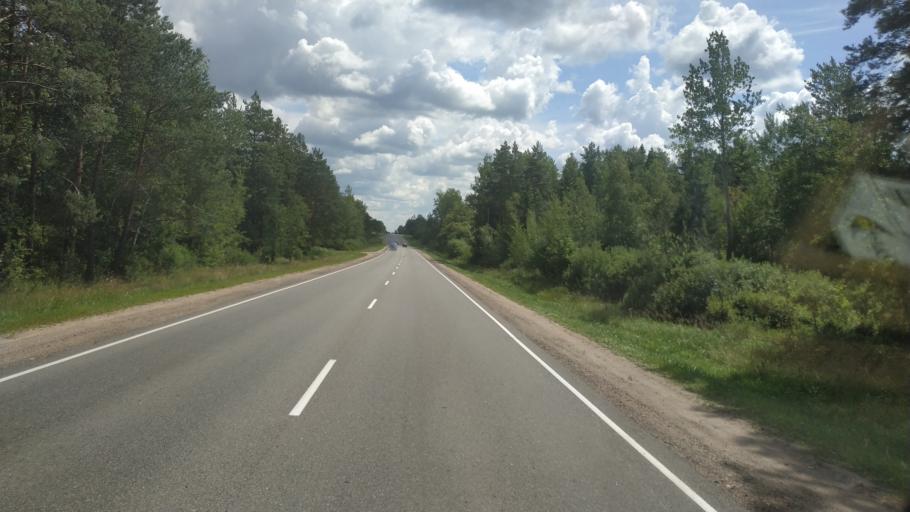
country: BY
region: Mogilev
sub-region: Mahilyowski Rayon
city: Veyno
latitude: 53.8235
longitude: 30.4268
